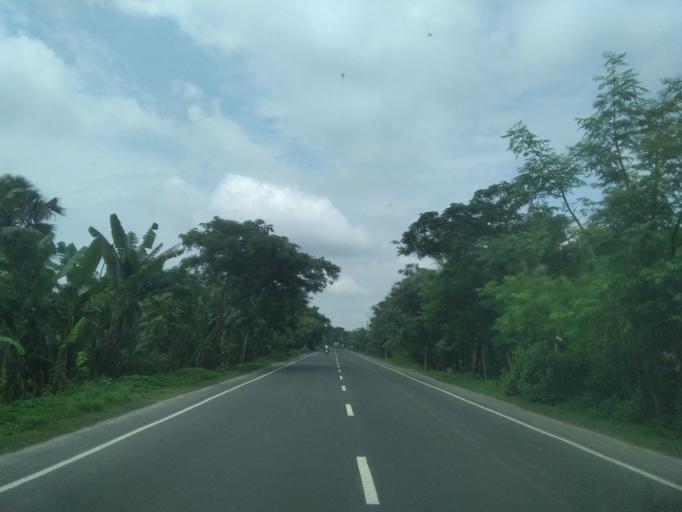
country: BD
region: Khulna
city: Kesabpur
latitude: 22.7986
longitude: 89.2293
